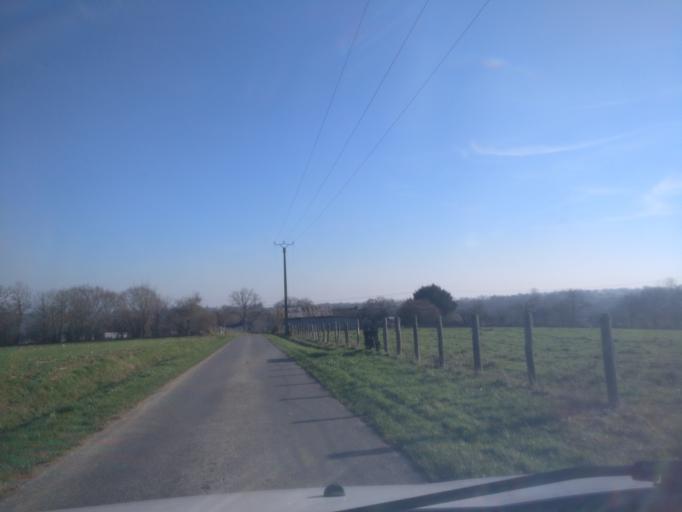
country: FR
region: Brittany
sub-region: Departement d'Ille-et-Vilaine
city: Livre-sur-Changeon
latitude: 48.2421
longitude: -1.3510
